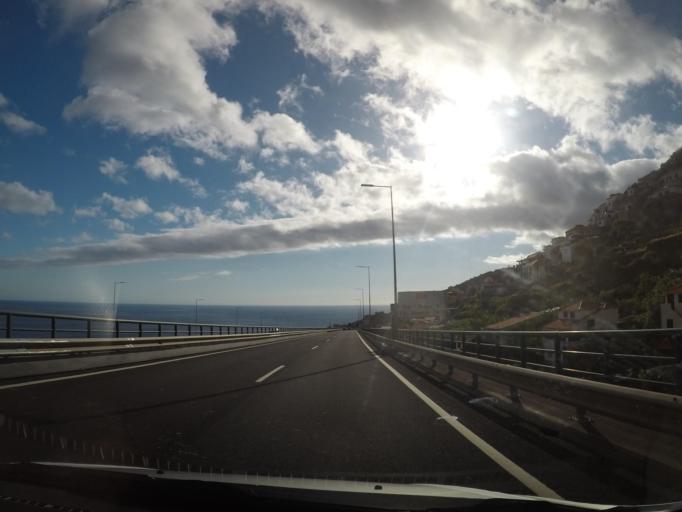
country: PT
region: Madeira
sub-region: Ribeira Brava
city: Campanario
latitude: 32.6645
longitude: -17.0365
